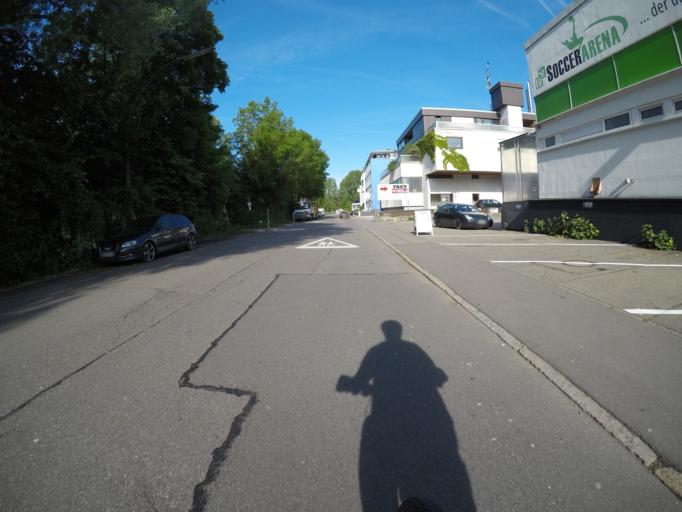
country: DE
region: Baden-Wuerttemberg
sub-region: Regierungsbezirk Stuttgart
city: Sindelfingen
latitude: 48.7047
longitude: 9.0158
